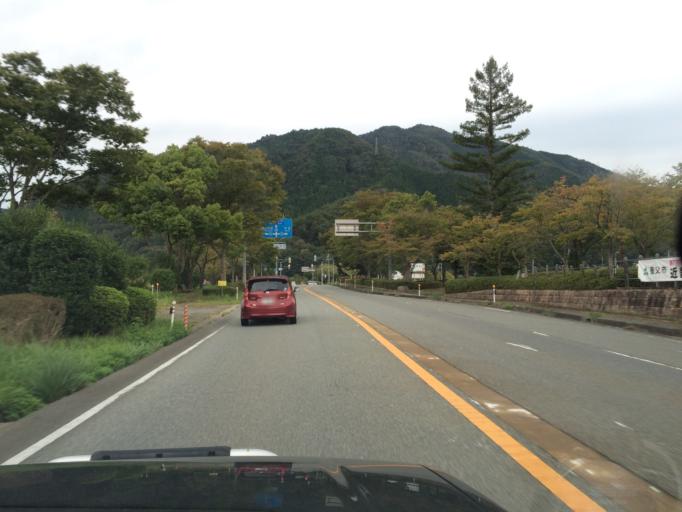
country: JP
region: Hyogo
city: Toyooka
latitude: 35.3834
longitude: 134.8159
